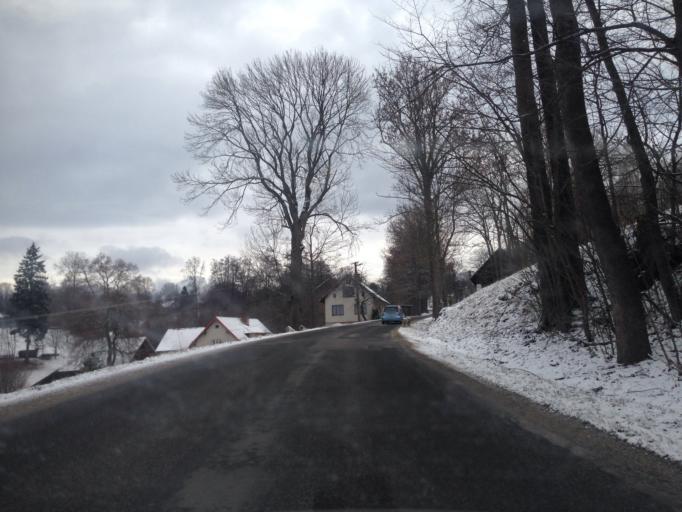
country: CZ
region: Liberecky
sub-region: Okres Semily
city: Vysoke nad Jizerou
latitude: 50.6587
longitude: 15.4159
